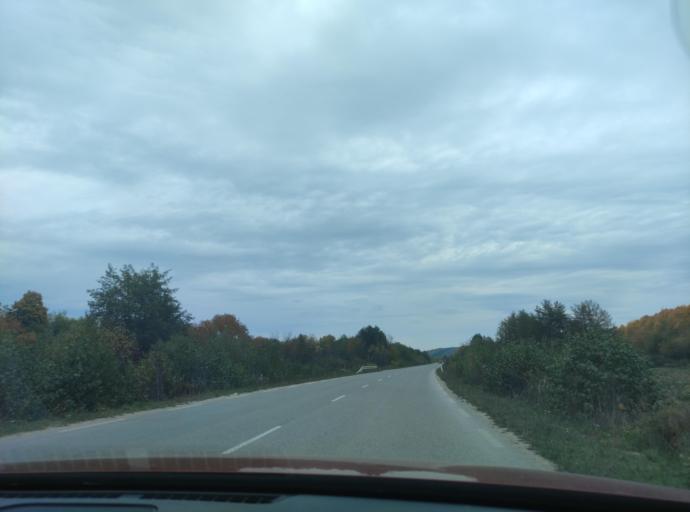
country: BG
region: Montana
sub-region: Obshtina Berkovitsa
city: Berkovitsa
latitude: 43.2359
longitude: 23.1598
